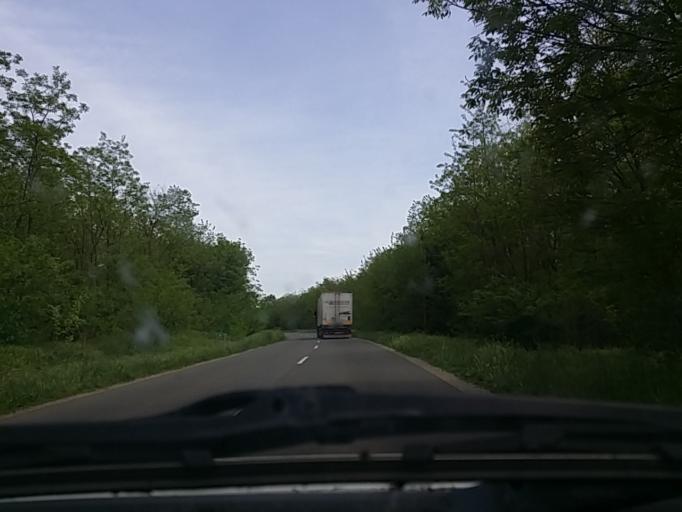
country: HU
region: Baranya
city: Vajszlo
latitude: 45.8723
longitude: 17.9519
